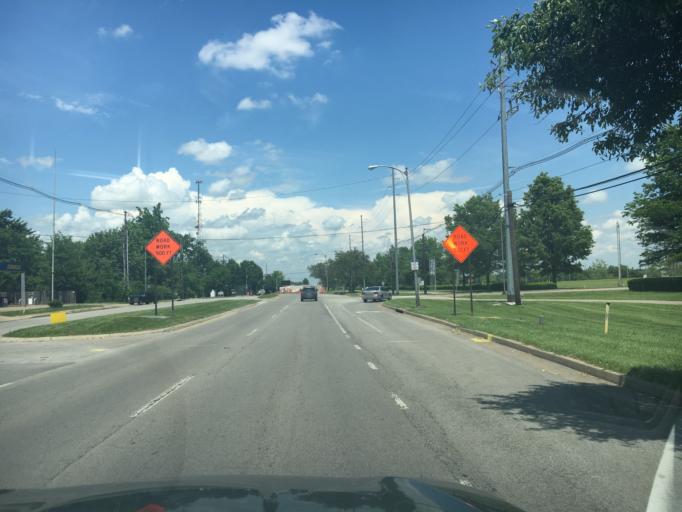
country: US
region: Kentucky
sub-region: Fayette County
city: Mount Vernon
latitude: 38.0687
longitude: -84.4976
